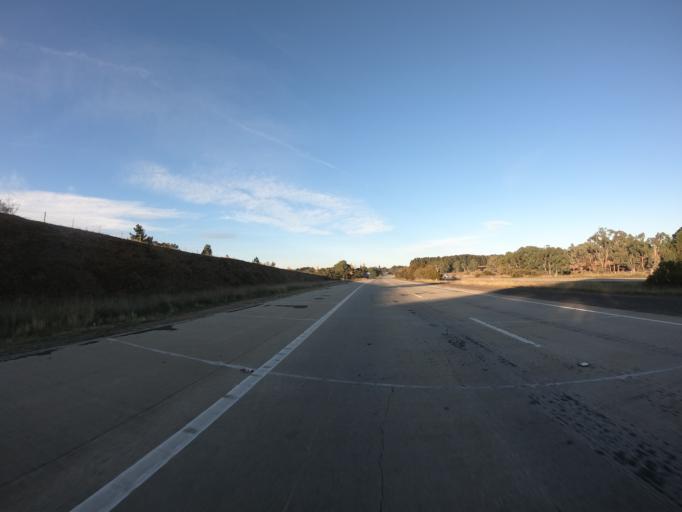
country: AU
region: New South Wales
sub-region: Yass Valley
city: Gundaroo
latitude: -35.1375
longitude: 149.3385
